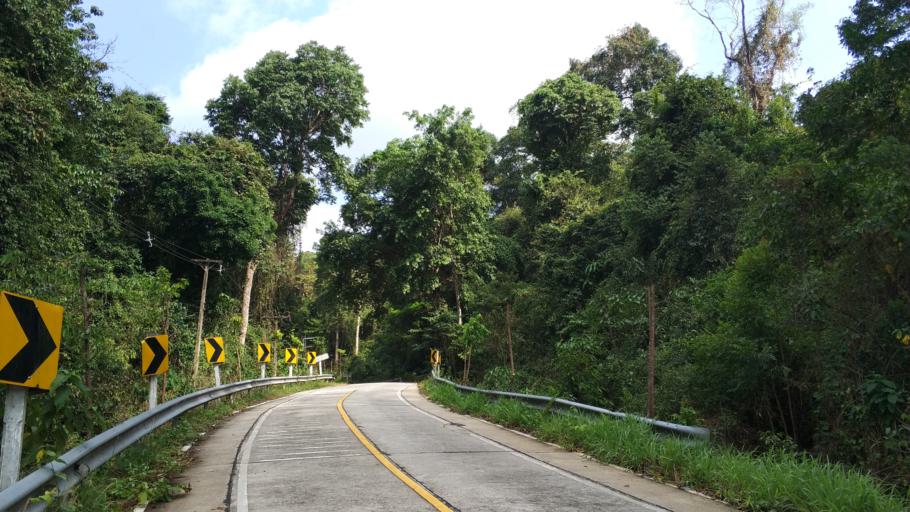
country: TH
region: Trat
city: Ko Kut
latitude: 11.6076
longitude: 102.5766
